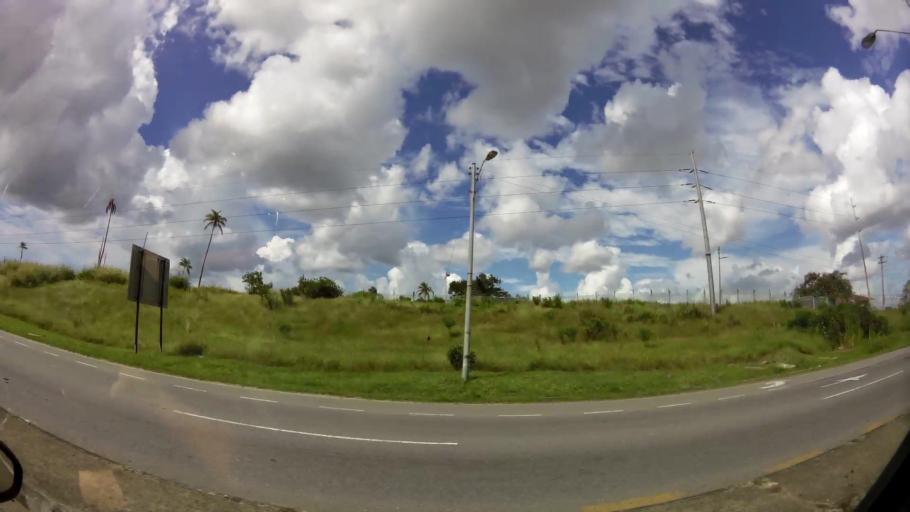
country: TT
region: City of San Fernando
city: San Fernando
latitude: 10.2600
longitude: -61.4625
